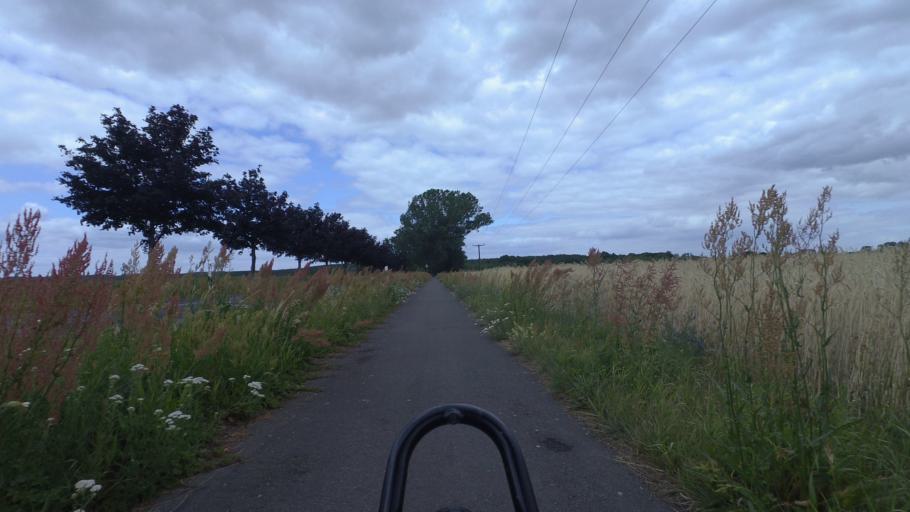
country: DE
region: Brandenburg
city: Trebbin
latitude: 52.2277
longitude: 13.1972
